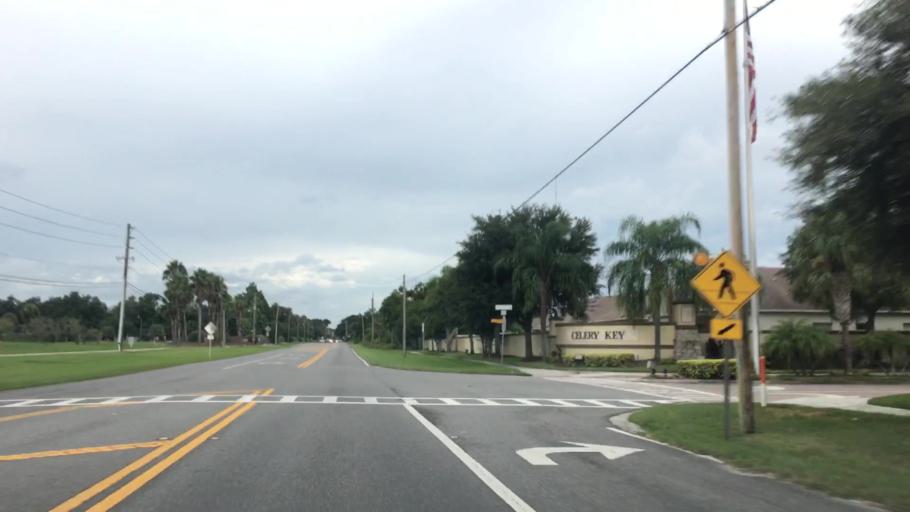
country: US
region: Florida
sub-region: Seminole County
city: Midway
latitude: 28.8014
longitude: -81.2462
